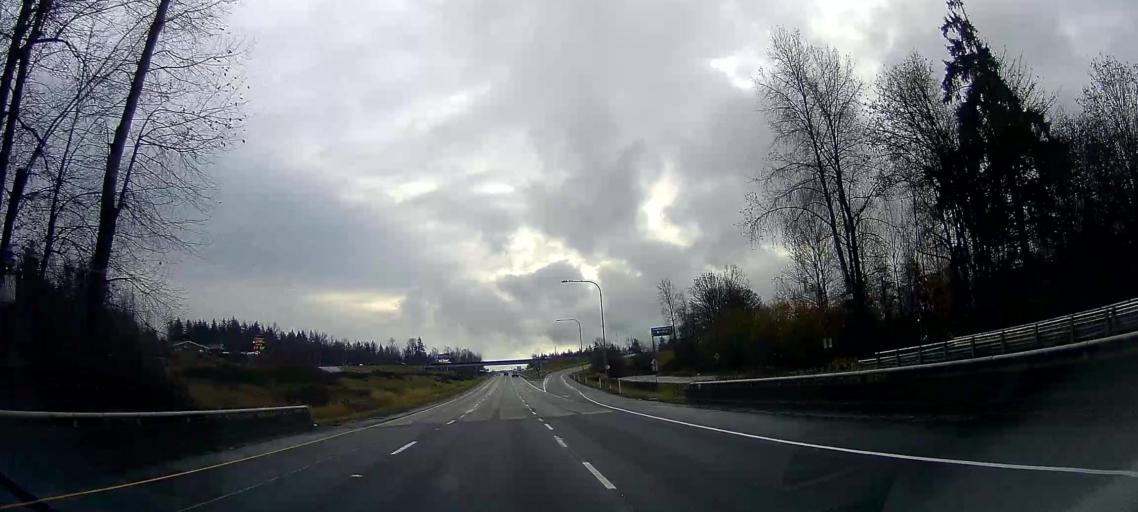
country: US
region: Washington
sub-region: Snohomish County
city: Bryant
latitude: 48.2138
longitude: -122.2185
